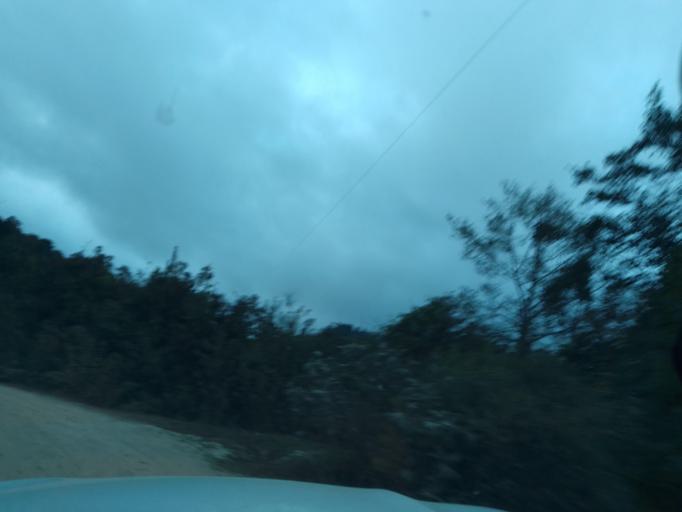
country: MX
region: Chiapas
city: Motozintla de Mendoza
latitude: 15.2223
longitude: -92.2361
